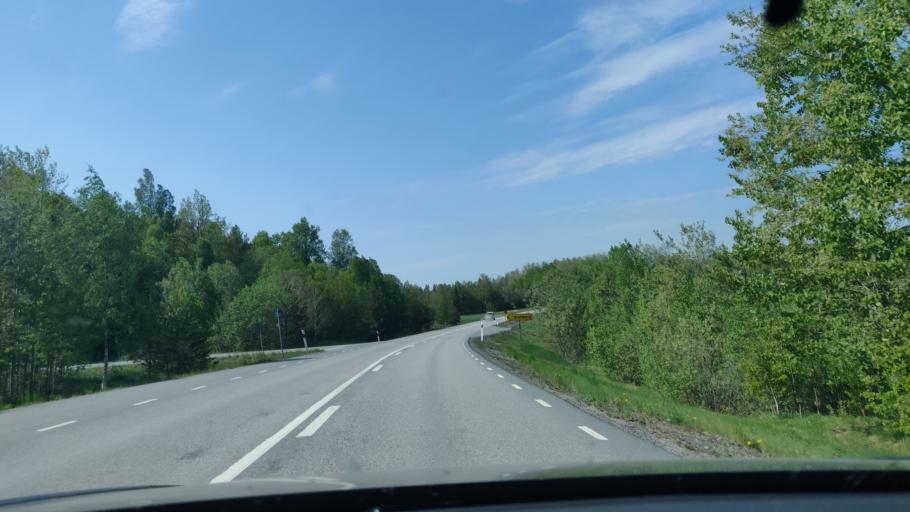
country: SE
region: Uppsala
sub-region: Heby Kommun
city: OEstervala
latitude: 60.1455
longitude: 17.2027
